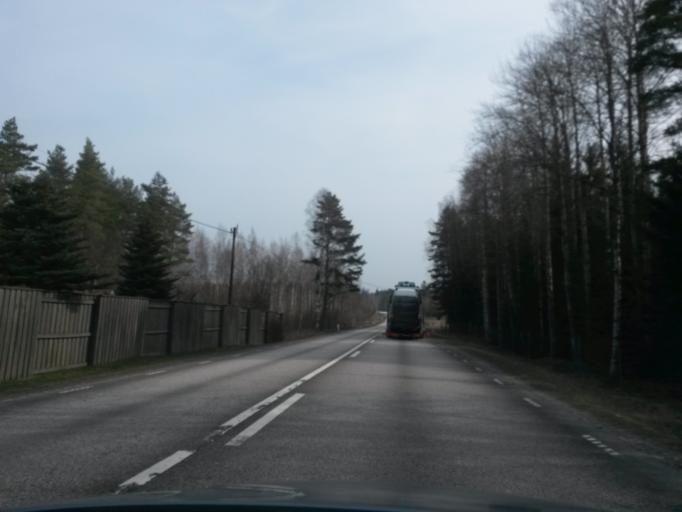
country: SE
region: Vaestra Goetaland
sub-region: Gullspangs Kommun
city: Hova
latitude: 58.8299
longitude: 14.1782
